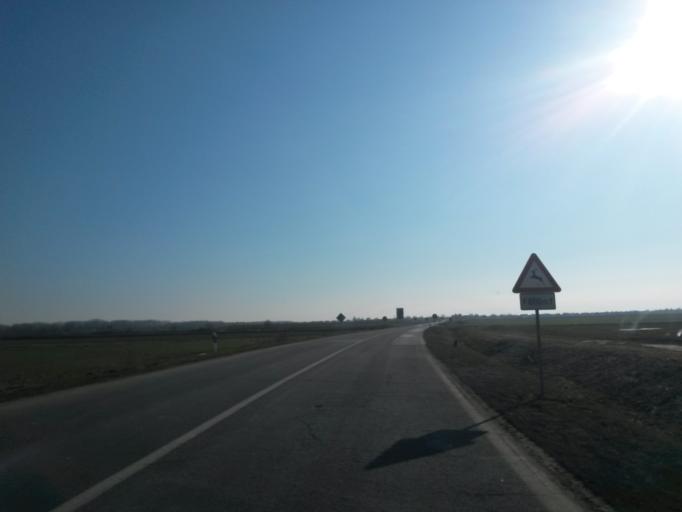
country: HR
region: Osjecko-Baranjska
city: Sarvas
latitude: 45.5341
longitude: 18.8143
